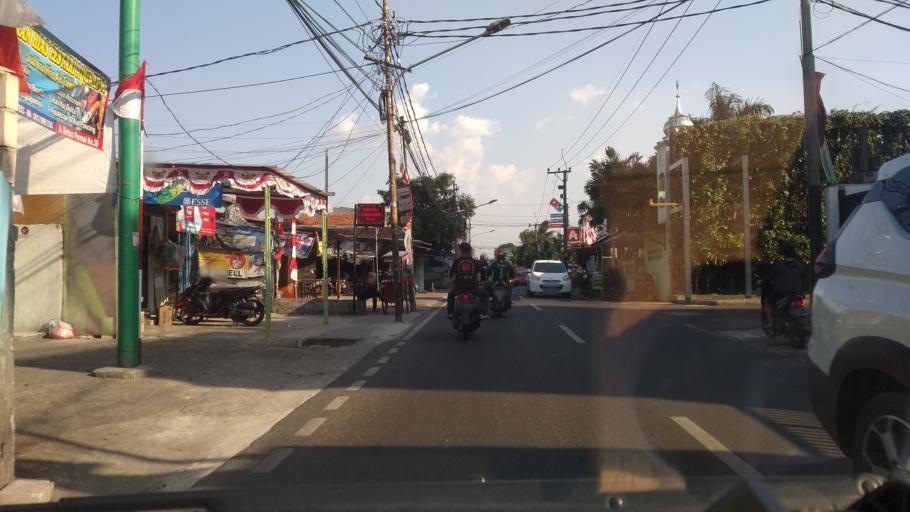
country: ID
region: Banten
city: South Tangerang
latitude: -6.2578
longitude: 106.7597
